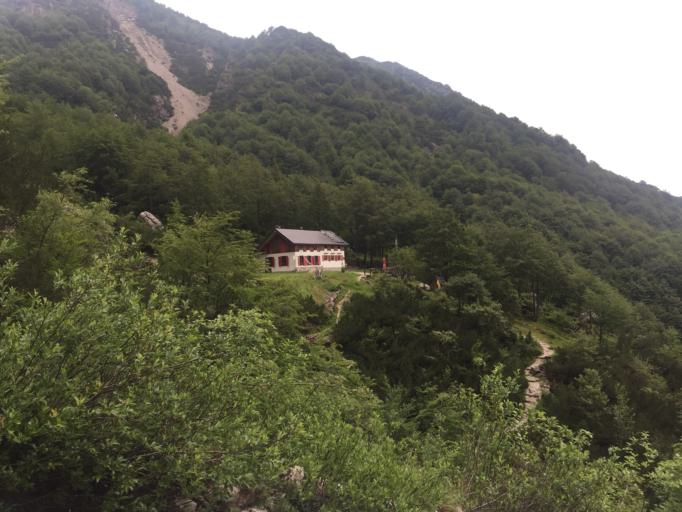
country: IT
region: Friuli Venezia Giulia
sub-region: Provincia di Udine
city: Paularo
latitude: 46.4759
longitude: 13.1599
